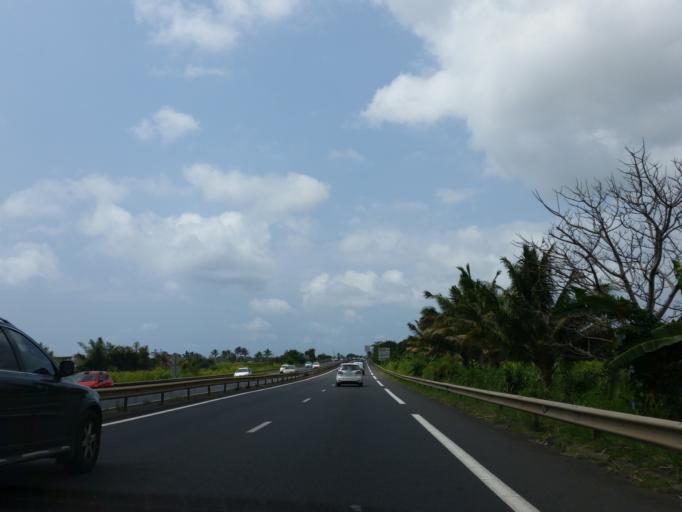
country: RE
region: Reunion
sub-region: Reunion
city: Sainte-Suzanne
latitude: -20.9144
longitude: 55.6110
